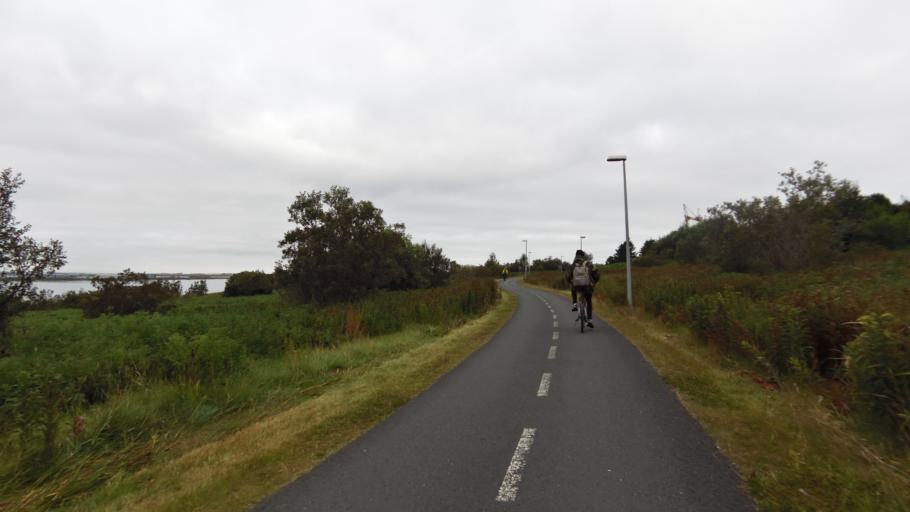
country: IS
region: Capital Region
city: Kopavogur
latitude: 64.1218
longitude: -21.9195
